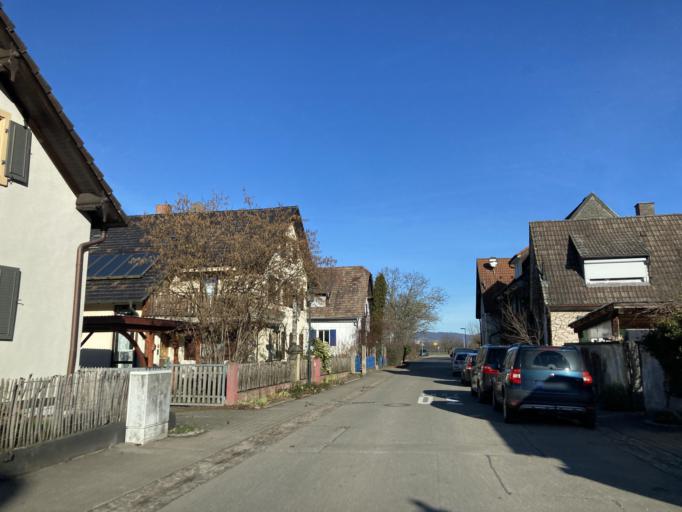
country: DE
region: Baden-Wuerttemberg
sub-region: Freiburg Region
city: Merdingen
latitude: 47.9882
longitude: 7.6710
